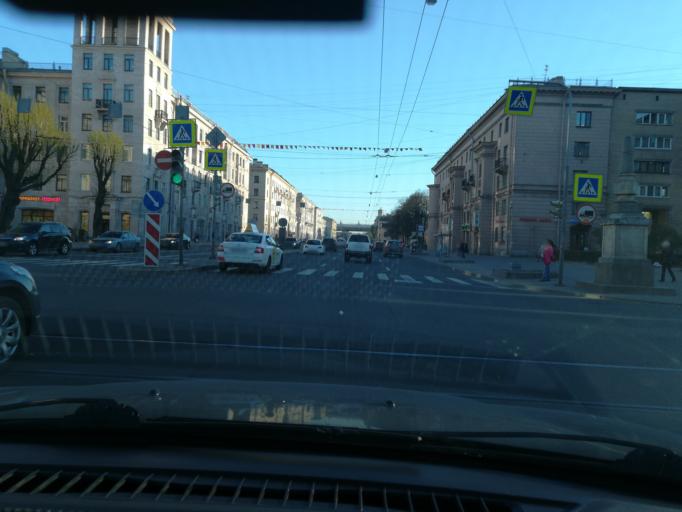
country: RU
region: St.-Petersburg
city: Avtovo
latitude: 59.8905
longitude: 30.2716
